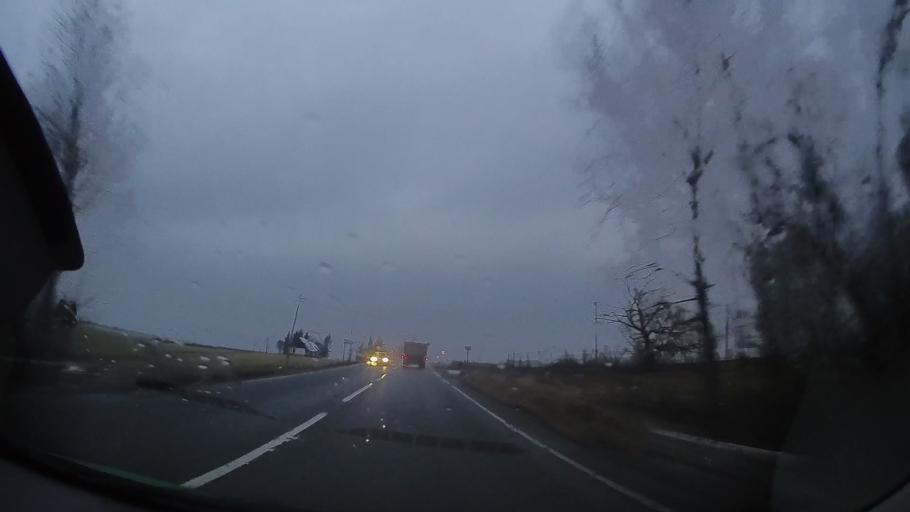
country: RO
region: Harghita
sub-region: Comuna Lazarea
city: Lazarea
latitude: 46.7660
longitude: 25.5122
